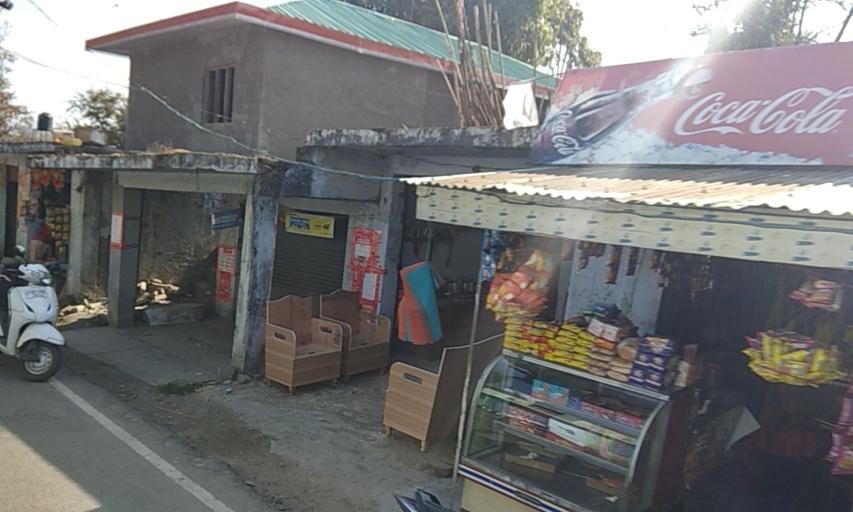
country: IN
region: Himachal Pradesh
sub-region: Kangra
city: Dharmsala
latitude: 32.1667
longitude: 76.3931
